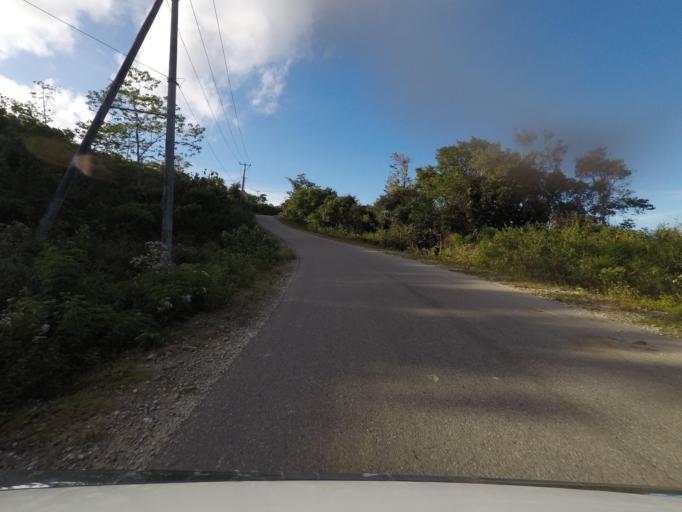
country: TL
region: Lautem
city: Lospalos
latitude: -8.4059
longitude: 127.0008
